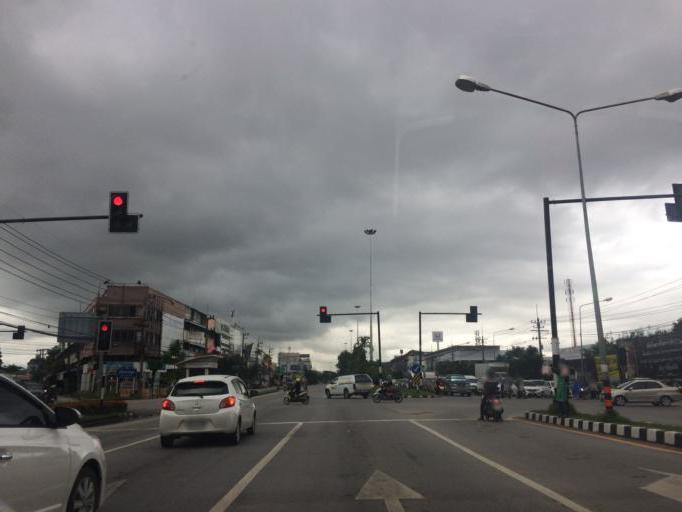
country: TH
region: Chiang Rai
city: Chiang Rai
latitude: 19.8979
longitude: 99.8389
